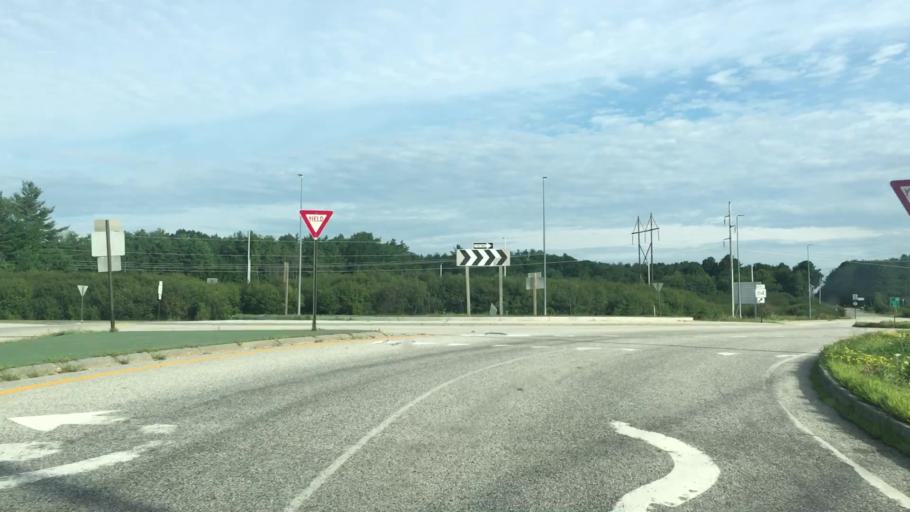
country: US
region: Maine
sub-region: Cumberland County
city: Gorham
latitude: 43.6518
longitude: -70.4271
